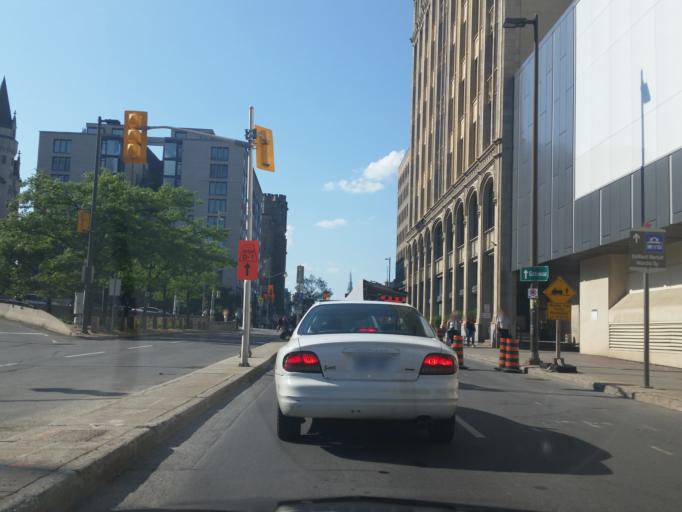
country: CA
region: Ontario
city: Ottawa
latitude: 45.4248
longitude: -75.6928
